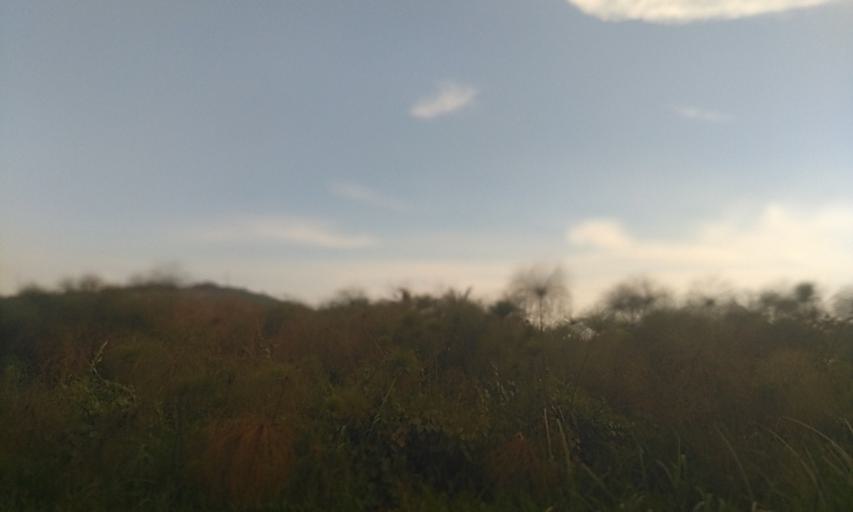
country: UG
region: Central Region
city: Kampala Central Division
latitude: 0.2957
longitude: 32.5229
